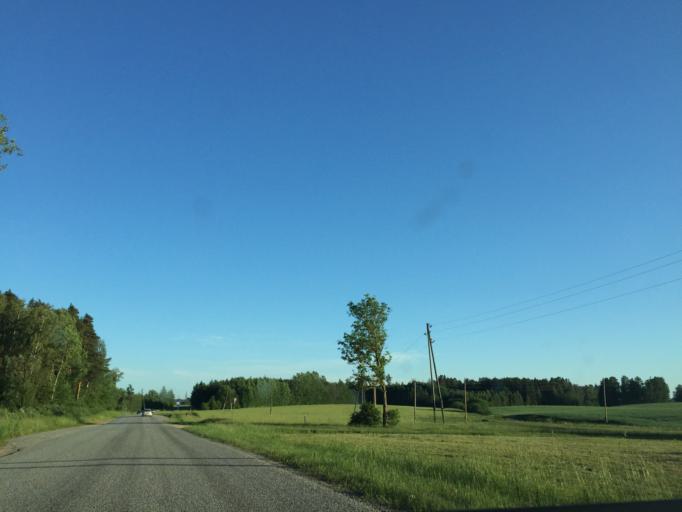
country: LV
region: Broceni
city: Broceni
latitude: 56.7016
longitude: 22.5052
